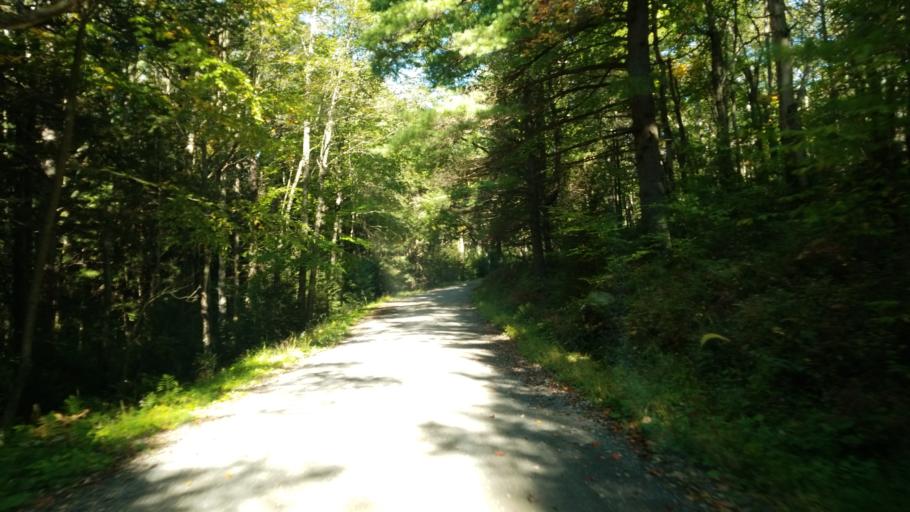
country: US
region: Pennsylvania
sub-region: Clearfield County
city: Hyde
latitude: 41.0868
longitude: -78.5330
